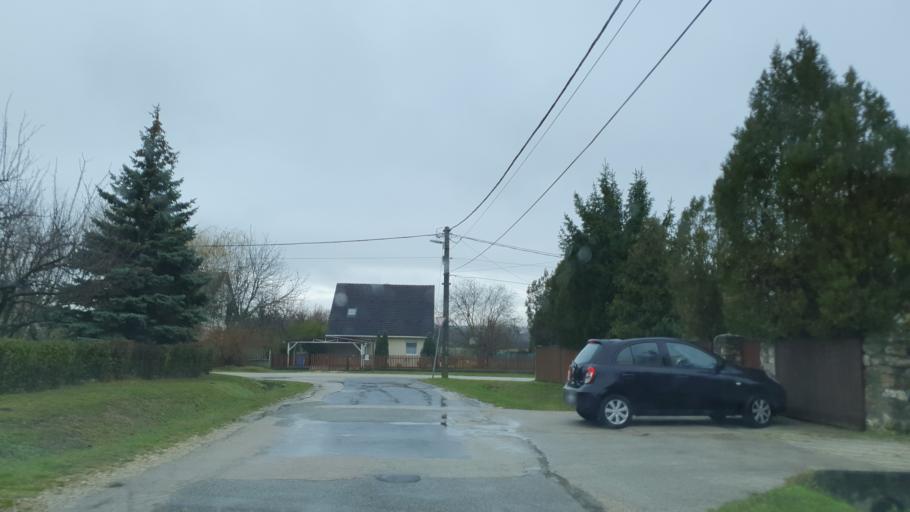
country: HU
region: Veszprem
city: Veszprem
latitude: 47.1351
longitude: 17.9436
